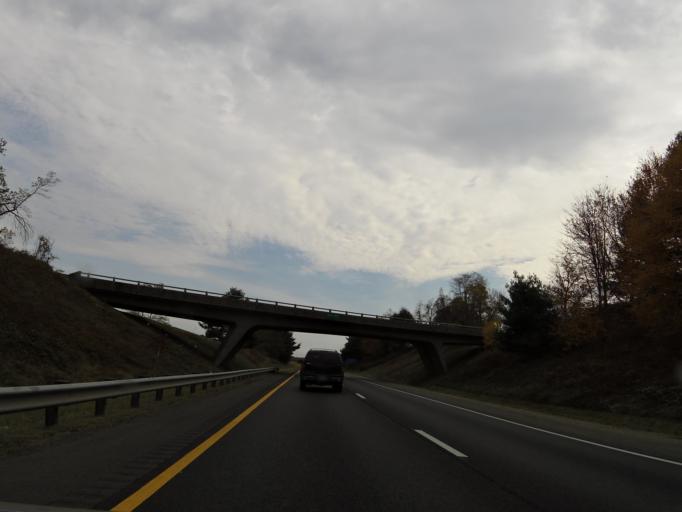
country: US
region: Virginia
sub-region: Carroll County
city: Woodlawn
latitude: 36.7692
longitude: -80.8052
